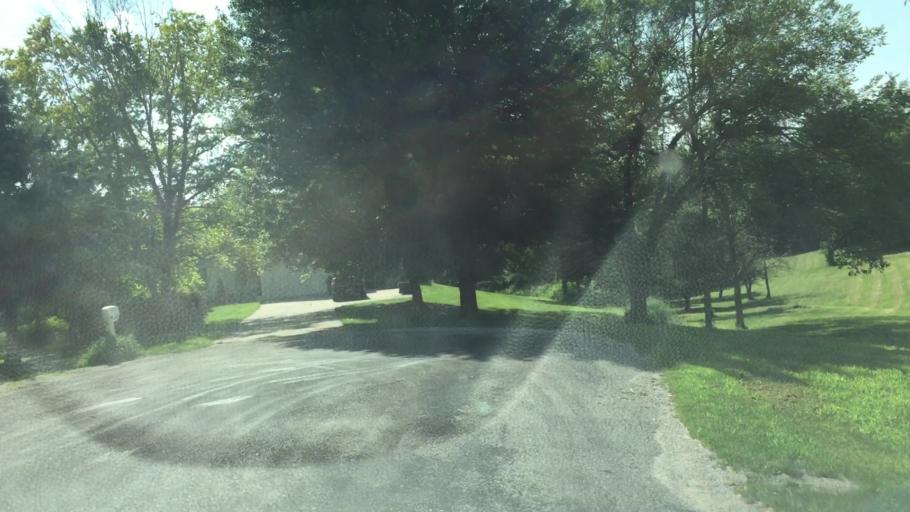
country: US
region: Iowa
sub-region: Johnson County
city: North Liberty
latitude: 41.8052
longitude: -91.6197
